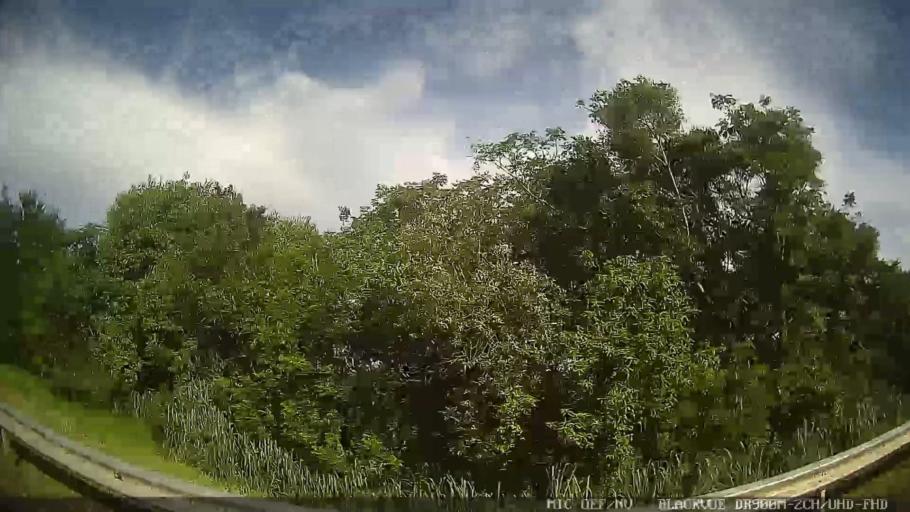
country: BR
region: Sao Paulo
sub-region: Tiete
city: Tiete
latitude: -23.1095
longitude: -47.6956
